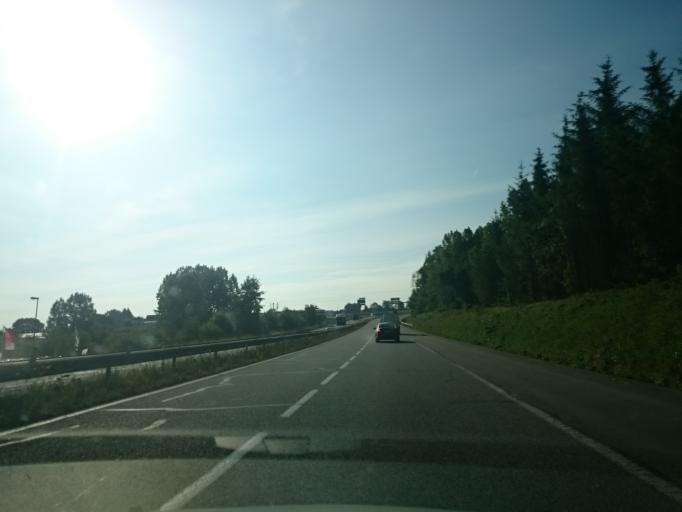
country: FR
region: Brittany
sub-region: Departement du Finistere
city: Ergue-Gaberic
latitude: 48.0033
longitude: -4.0574
